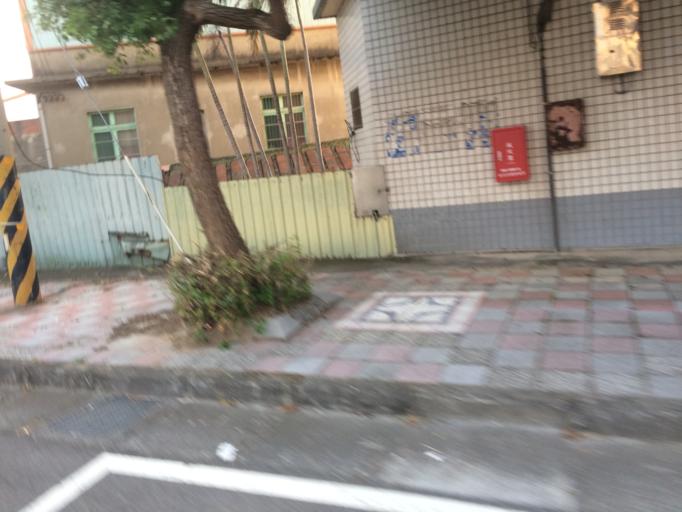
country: TW
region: Taiwan
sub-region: Hsinchu
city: Hsinchu
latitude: 24.7285
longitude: 120.9172
